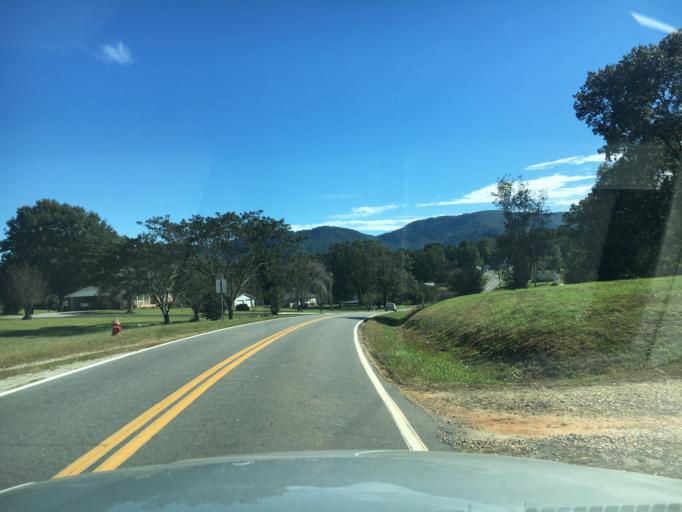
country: US
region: North Carolina
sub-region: Burke County
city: Salem
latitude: 35.6902
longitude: -81.7338
